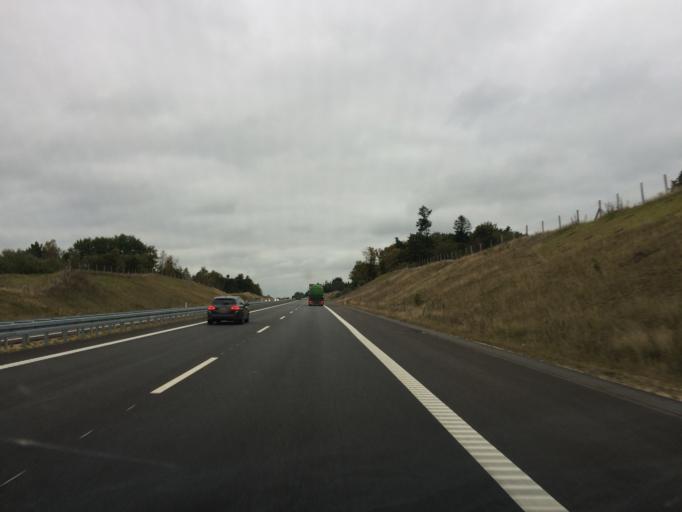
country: DK
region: Central Jutland
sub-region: Silkeborg Kommune
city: Silkeborg
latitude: 56.1788
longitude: 9.4814
